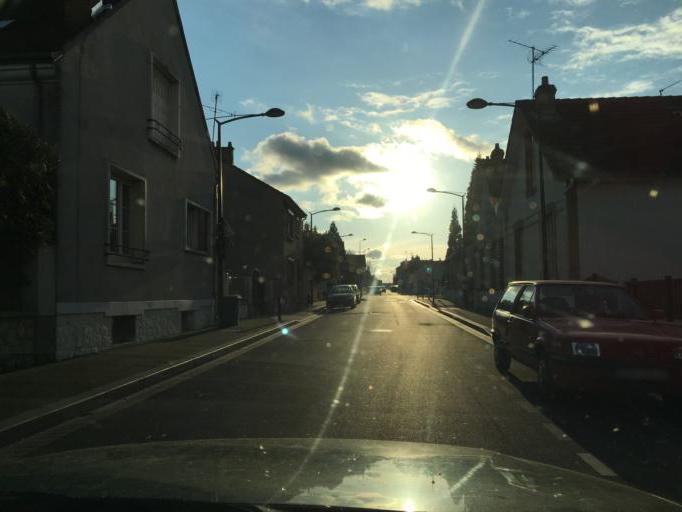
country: FR
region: Centre
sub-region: Departement du Loiret
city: Fleury-les-Aubrais
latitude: 47.9147
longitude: 1.9249
